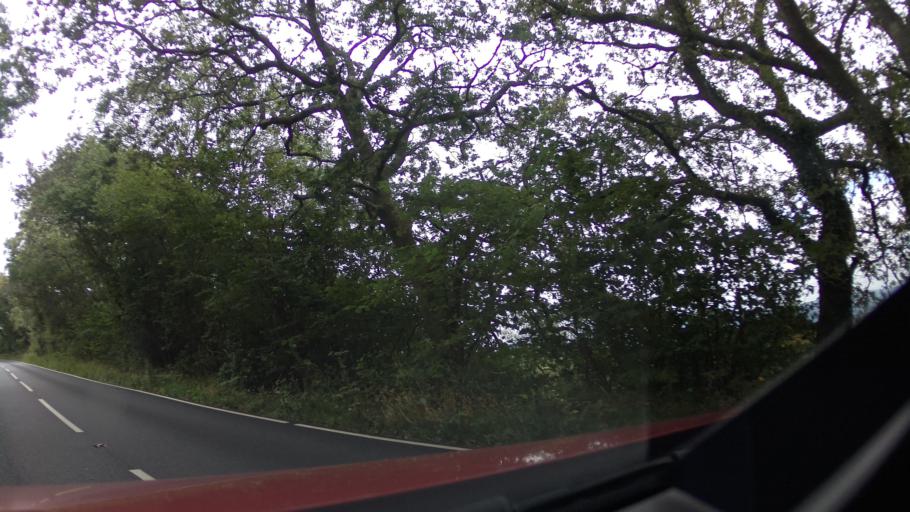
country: GB
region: England
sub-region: Devon
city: Bishopsteignton
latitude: 50.5852
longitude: -3.5315
